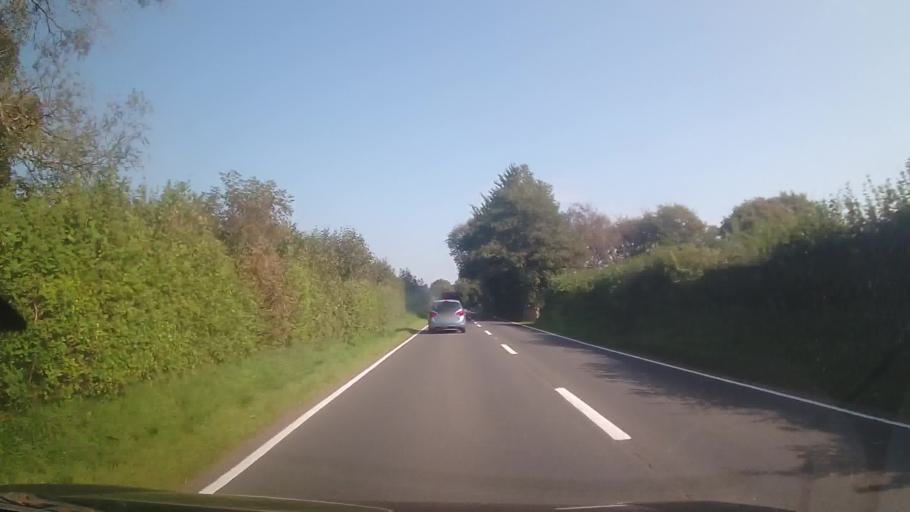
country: GB
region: Wales
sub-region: Pembrokeshire
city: Newport
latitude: 52.0159
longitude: -4.8202
